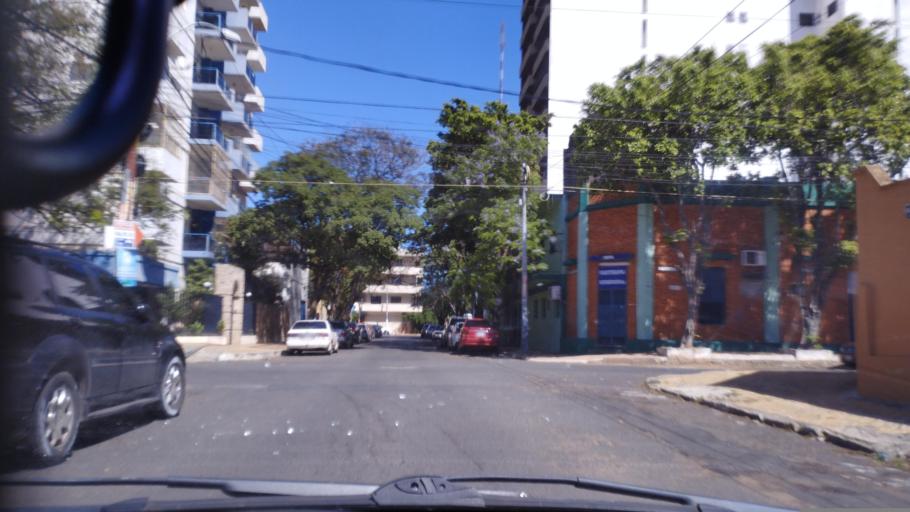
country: PY
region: Asuncion
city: Asuncion
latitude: -25.2900
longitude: -57.6463
